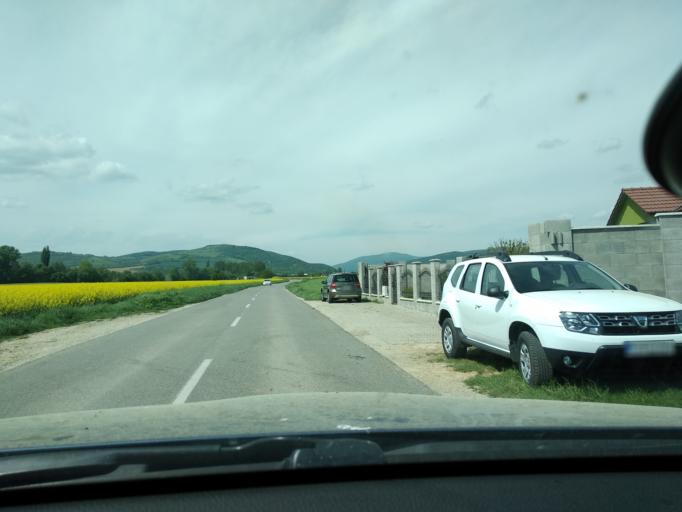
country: SK
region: Trenciansky
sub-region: Okres Nove Mesto nad Vahom
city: Nove Mesto nad Vahom
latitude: 48.8082
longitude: 17.8563
